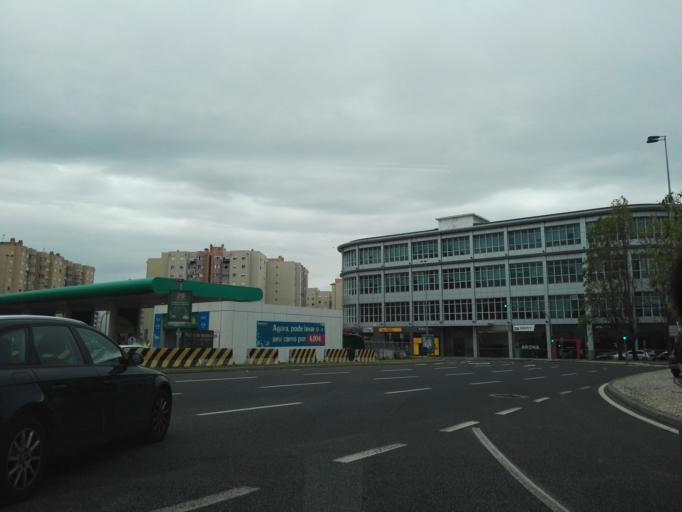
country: PT
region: Lisbon
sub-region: Loures
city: Moscavide
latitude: 38.7738
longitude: -9.1059
